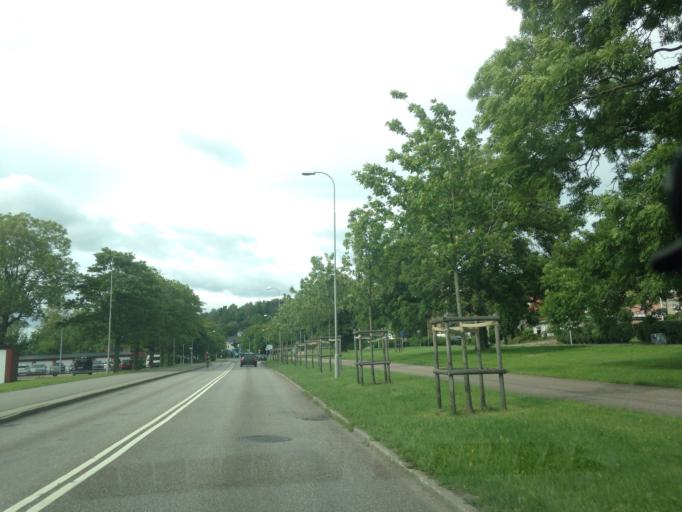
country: SE
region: Vaestra Goetaland
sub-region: Goteborg
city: Goeteborg
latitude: 57.7292
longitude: 11.9743
